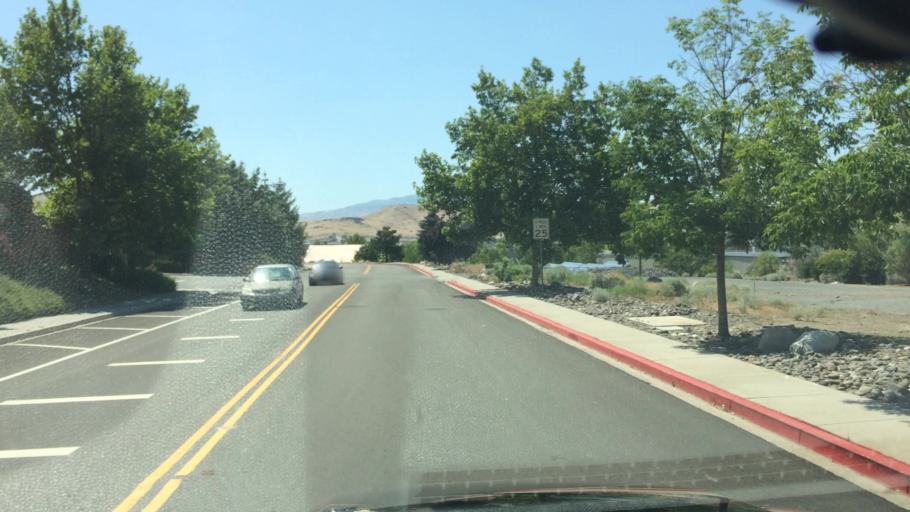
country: US
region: Nevada
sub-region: Washoe County
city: Sparks
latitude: 39.5777
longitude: -119.7150
